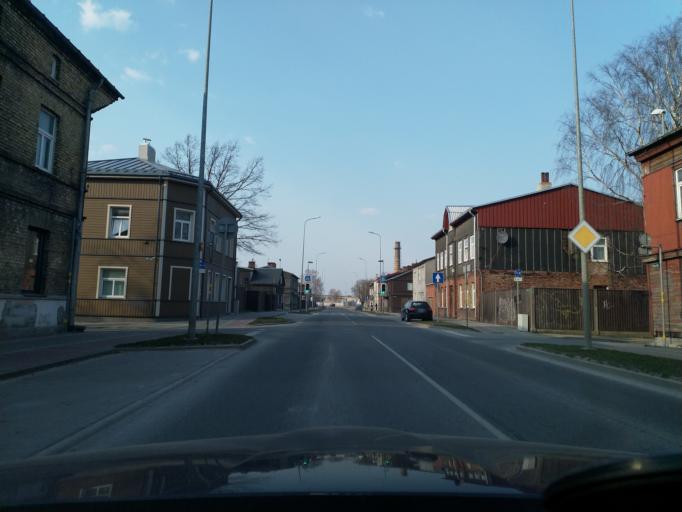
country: LV
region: Liepaja
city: Liepaja
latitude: 56.5072
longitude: 21.0252
